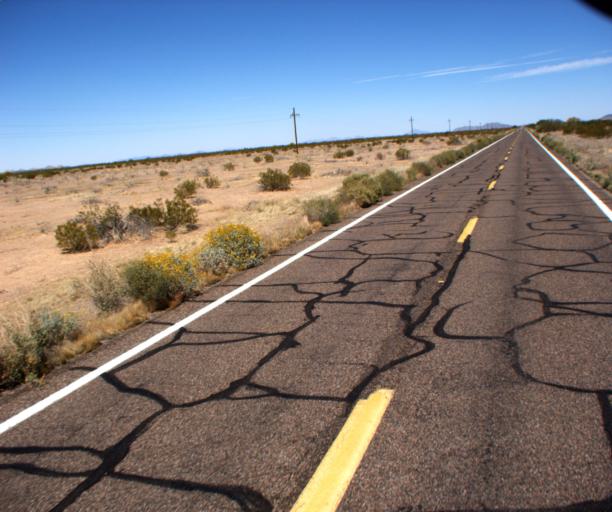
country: US
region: Arizona
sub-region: Pima County
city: Ajo
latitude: 32.5873
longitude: -112.8726
